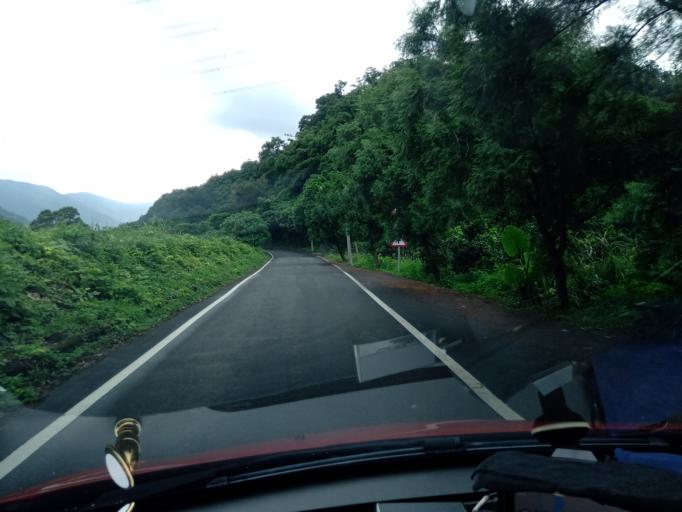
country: TW
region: Taiwan
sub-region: Yilan
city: Yilan
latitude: 24.7810
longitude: 121.7123
